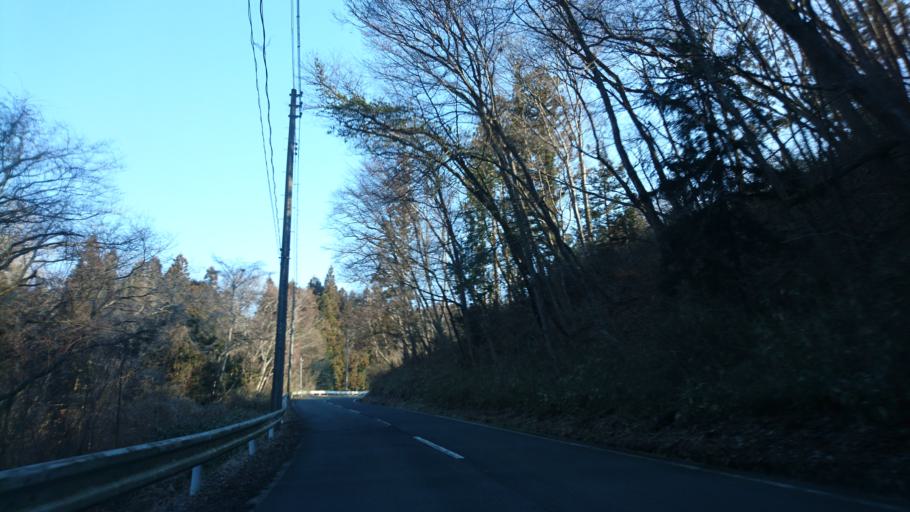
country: JP
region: Iwate
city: Ichinoseki
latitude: 38.9131
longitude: 141.2784
